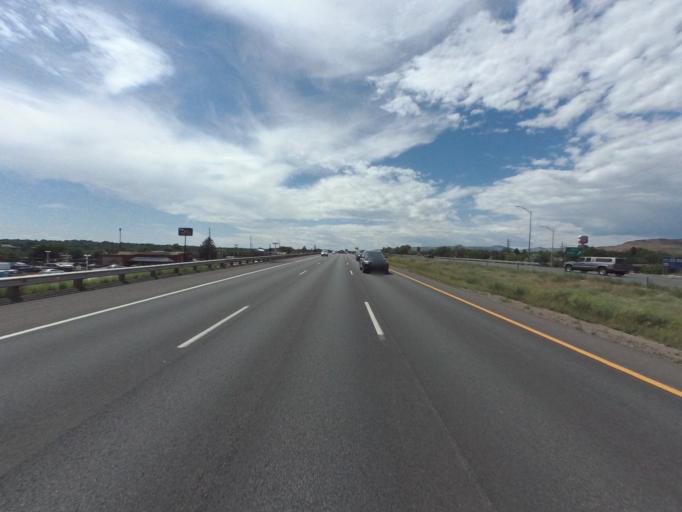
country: US
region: Colorado
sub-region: Jefferson County
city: Applewood
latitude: 39.7630
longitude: -105.1429
